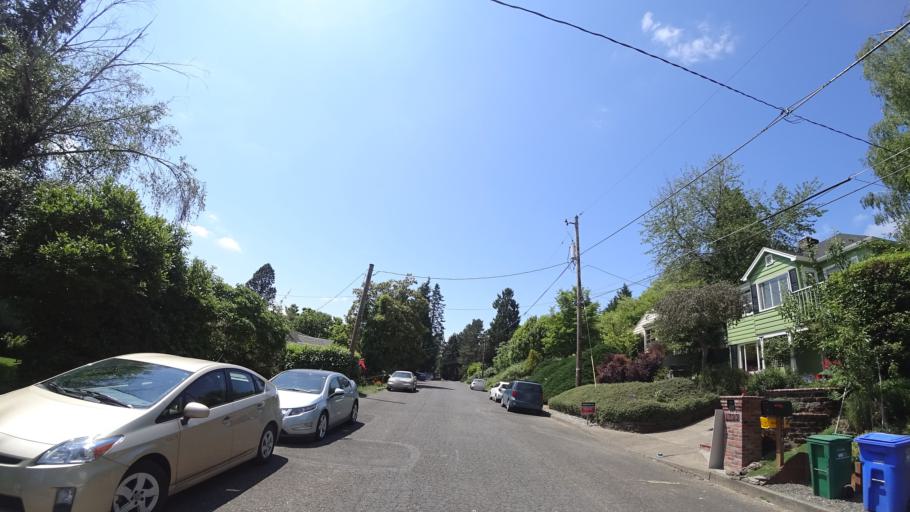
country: US
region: Oregon
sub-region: Clackamas County
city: Lake Oswego
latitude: 45.4683
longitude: -122.6956
